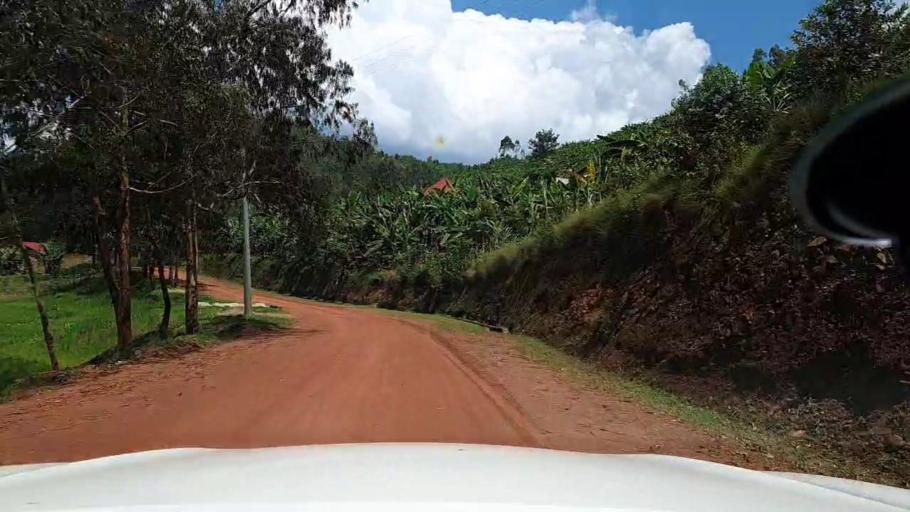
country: RW
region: Northern Province
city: Byumba
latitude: -1.6992
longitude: 29.8308
